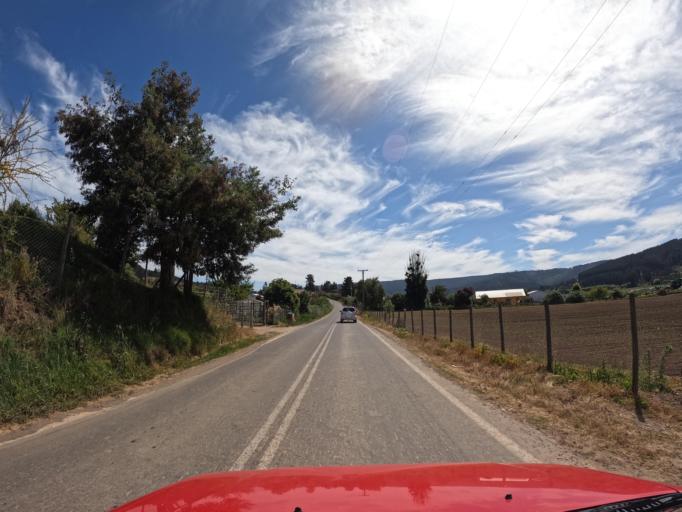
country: CL
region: Maule
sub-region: Provincia de Talca
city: Constitucion
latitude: -34.9913
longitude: -72.0020
